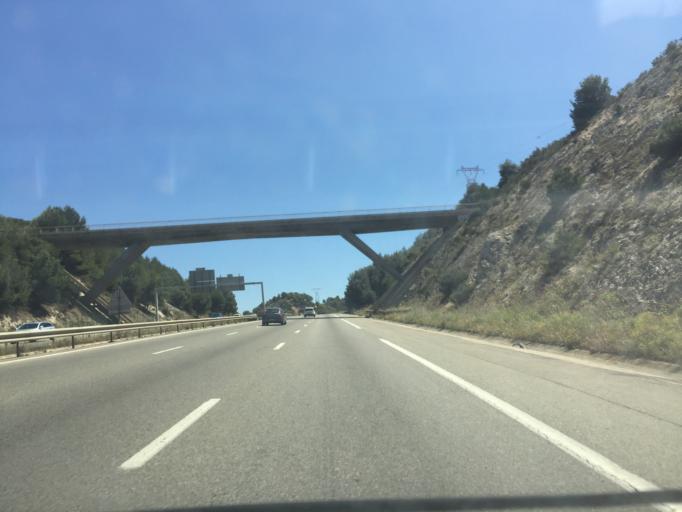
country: FR
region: Provence-Alpes-Cote d'Azur
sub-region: Departement des Bouches-du-Rhone
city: Les Pennes-Mirabeau
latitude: 43.3897
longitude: 5.3031
